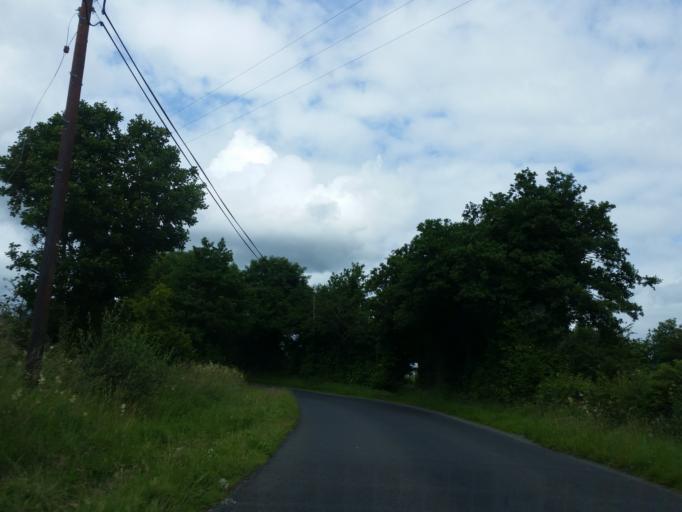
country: IE
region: Ulster
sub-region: County Monaghan
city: Clones
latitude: 54.2413
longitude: -7.2649
